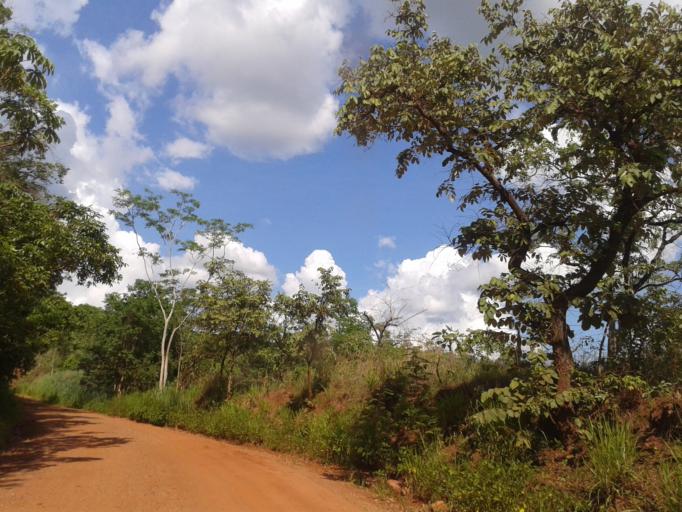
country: BR
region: Minas Gerais
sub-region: Campina Verde
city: Campina Verde
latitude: -19.3176
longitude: -49.8130
